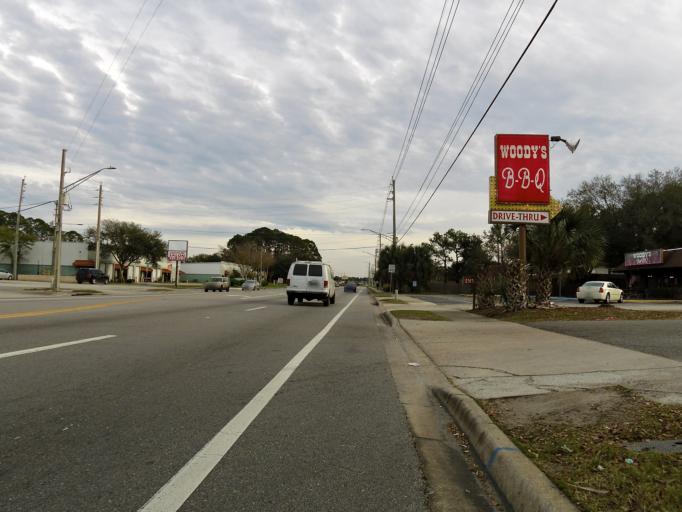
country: US
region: Florida
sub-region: Duval County
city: Jacksonville
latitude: 30.2633
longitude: -81.6219
